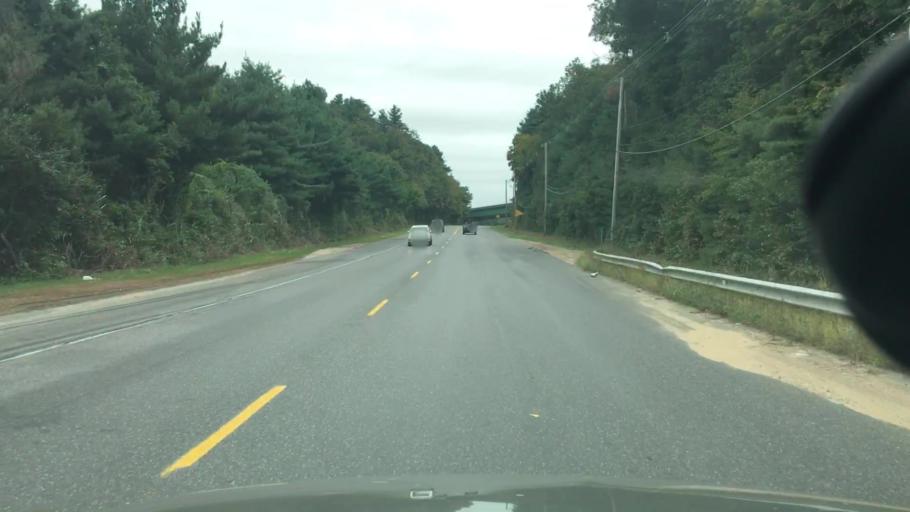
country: US
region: Massachusetts
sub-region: Worcester County
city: Sturbridge
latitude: 42.0678
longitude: -72.1059
